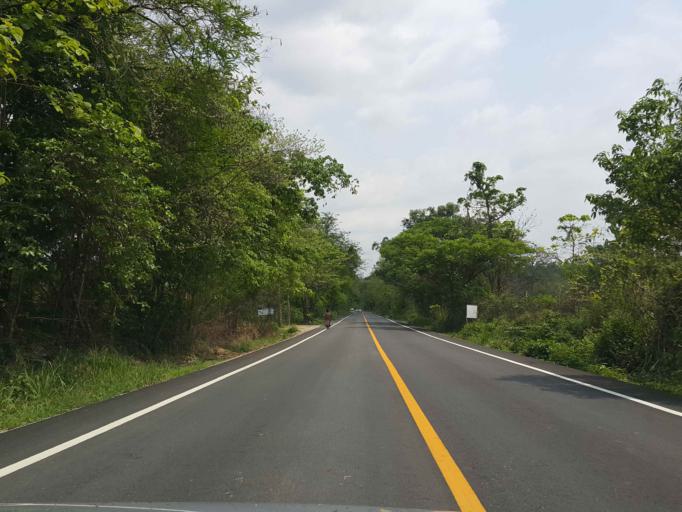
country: TH
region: Lampang
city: Thoen
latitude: 17.5627
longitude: 99.3323
